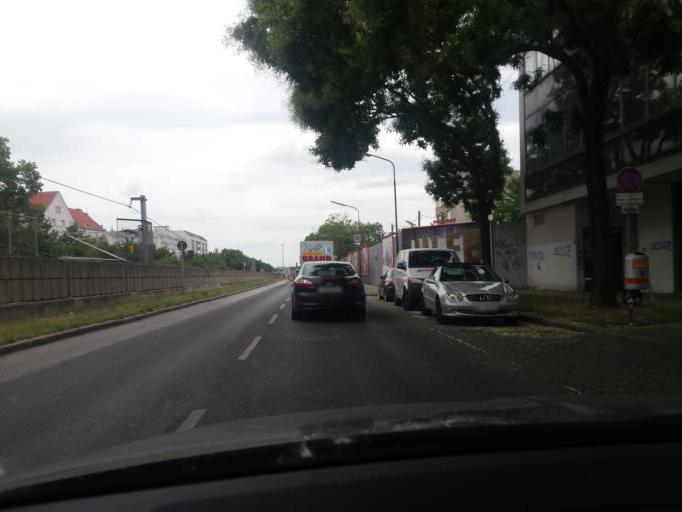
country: AT
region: Vienna
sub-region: Wien Stadt
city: Vienna
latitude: 48.1716
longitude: 16.4084
